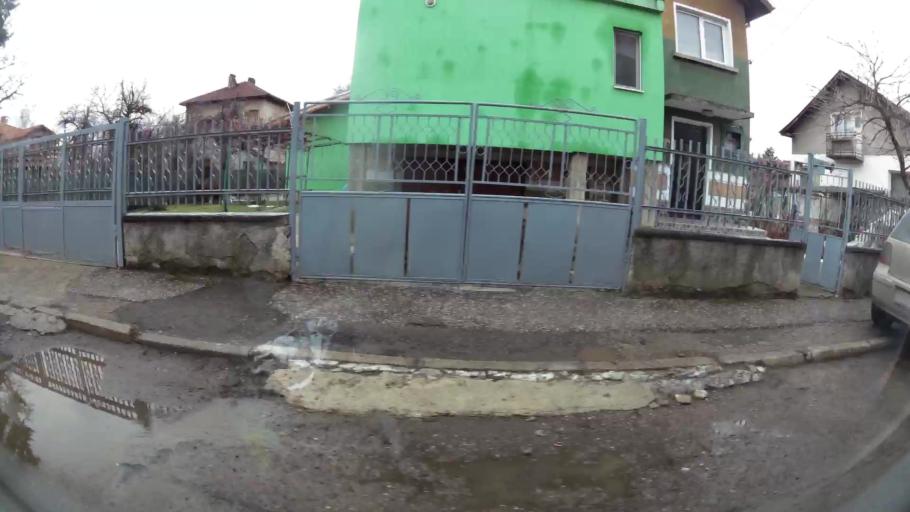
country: BG
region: Sofiya
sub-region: Obshtina Bozhurishte
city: Bozhurishte
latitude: 42.7436
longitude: 23.2630
